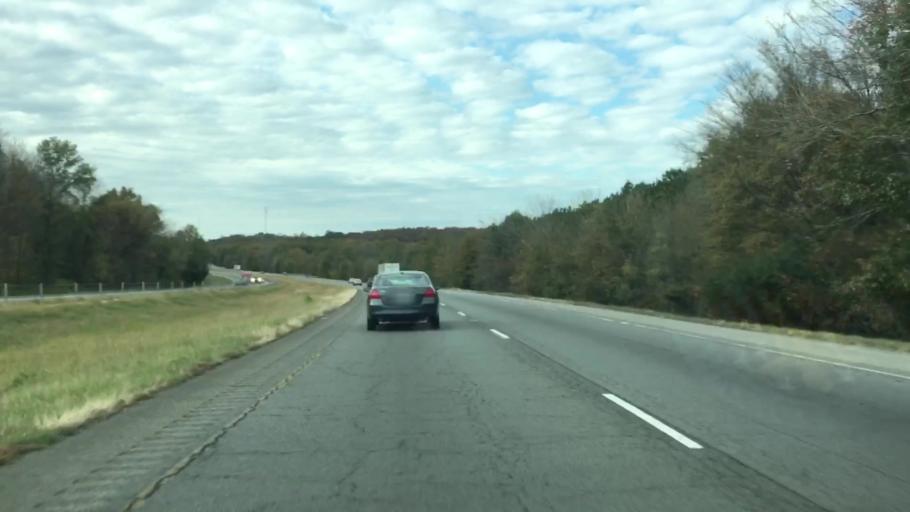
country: US
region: Arkansas
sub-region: Faulkner County
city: Conway
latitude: 35.1366
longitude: -92.5205
